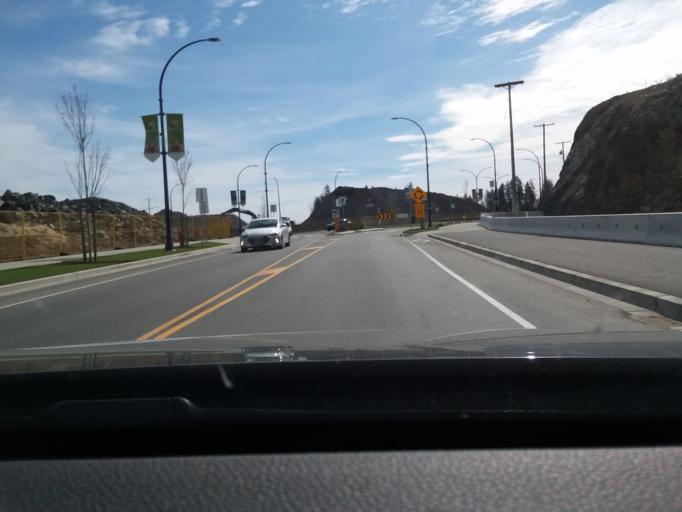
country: CA
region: British Columbia
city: Langford
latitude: 48.4491
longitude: -123.5410
